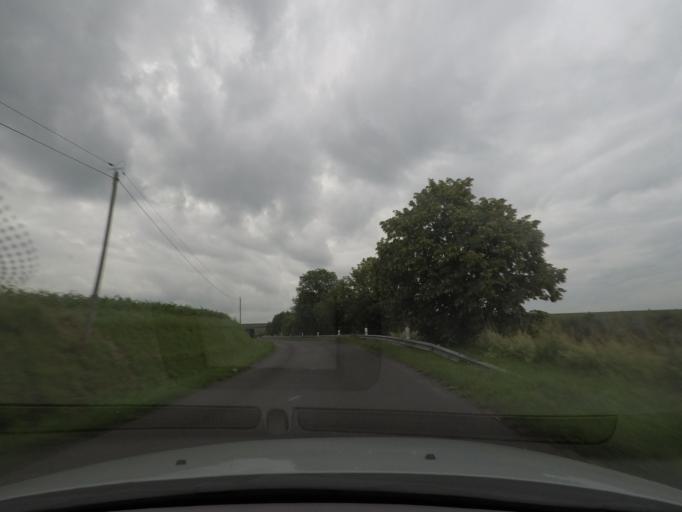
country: FR
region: Haute-Normandie
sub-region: Departement de la Seine-Maritime
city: Neufchatel-en-Bray
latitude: 49.7304
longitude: 1.4569
